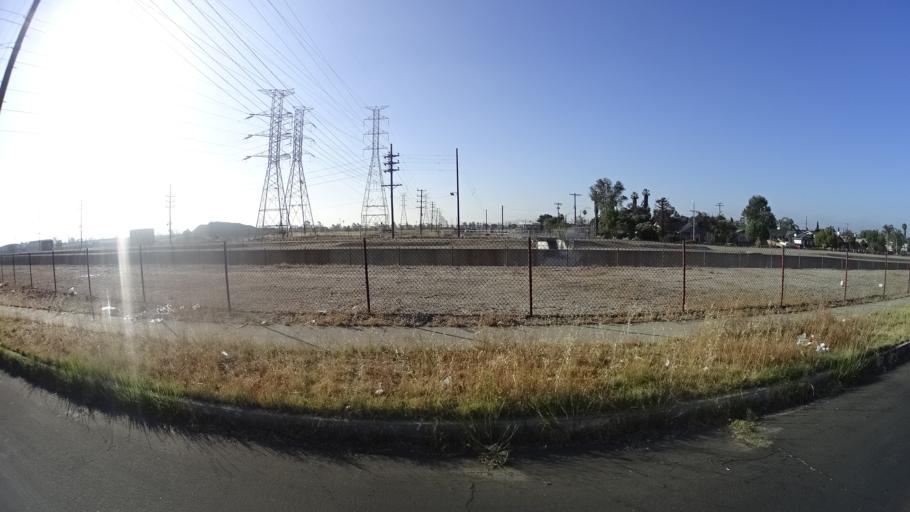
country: US
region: California
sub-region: Los Angeles County
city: Van Nuys
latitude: 34.2260
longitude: -118.4204
